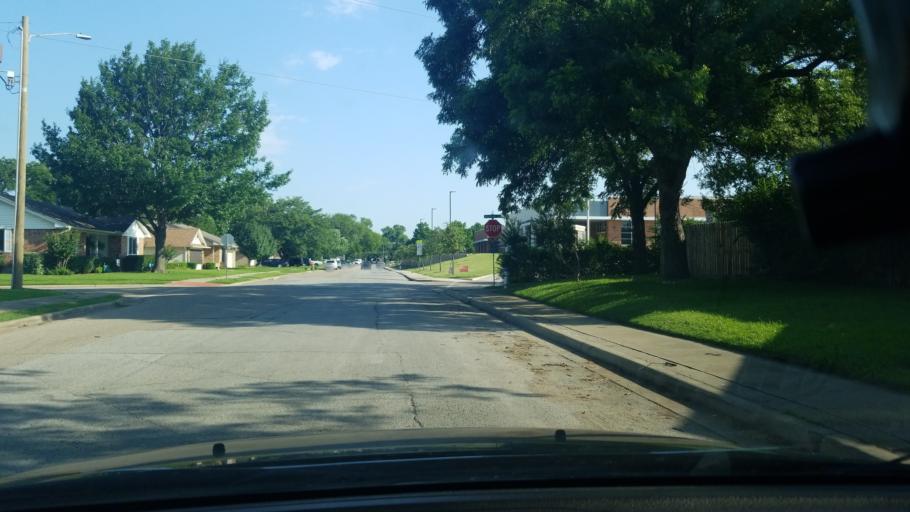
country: US
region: Texas
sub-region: Dallas County
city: Mesquite
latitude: 32.8268
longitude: -96.6381
